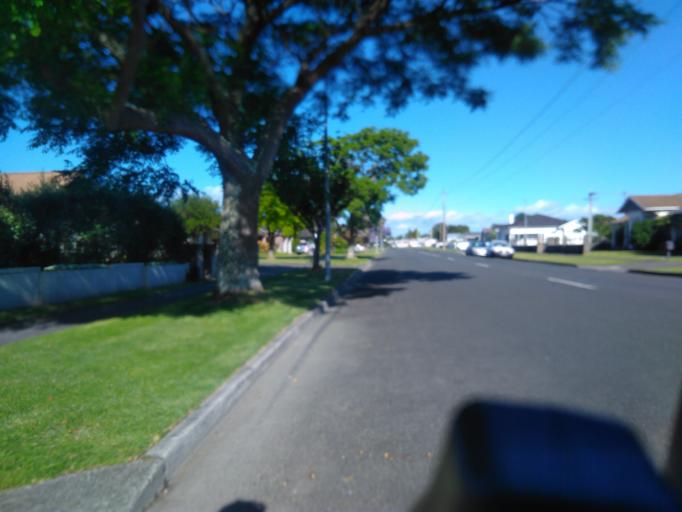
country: NZ
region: Gisborne
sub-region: Gisborne District
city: Gisborne
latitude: -38.6659
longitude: 178.0183
